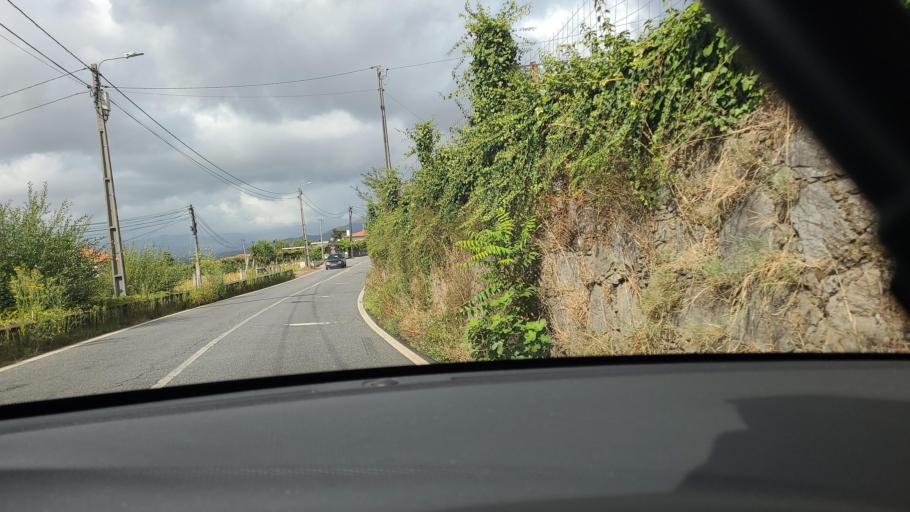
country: PT
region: Braga
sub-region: Braga
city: Adaufe
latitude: 41.5787
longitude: -8.4092
